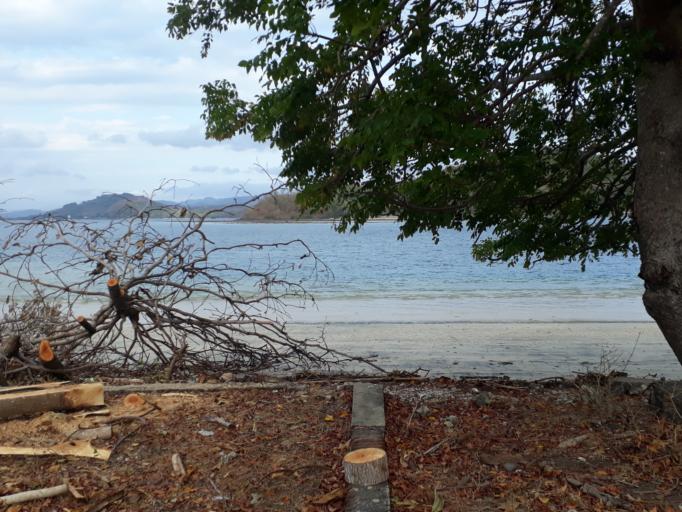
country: ID
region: West Nusa Tenggara
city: Tawun
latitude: -8.7442
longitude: 115.8908
